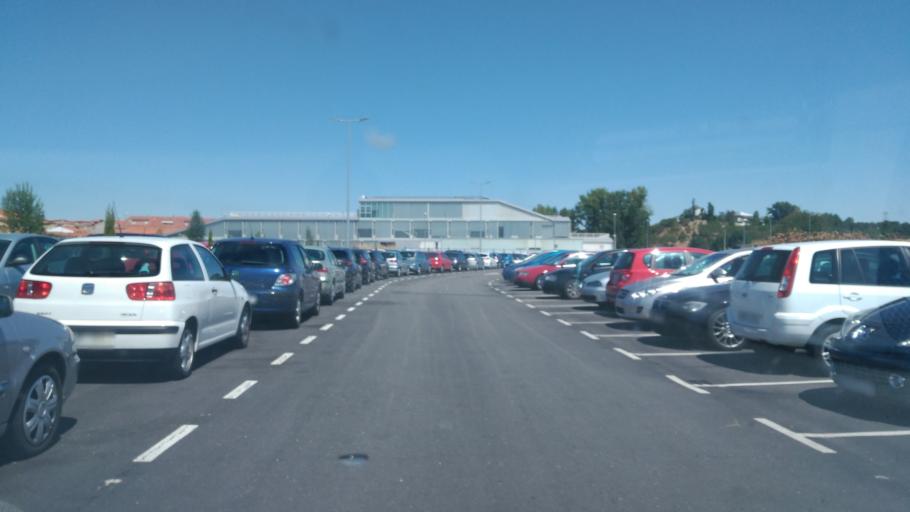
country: ES
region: Castille and Leon
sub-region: Provincia de Salamanca
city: Aldeatejada
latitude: 40.9187
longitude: -5.6929
